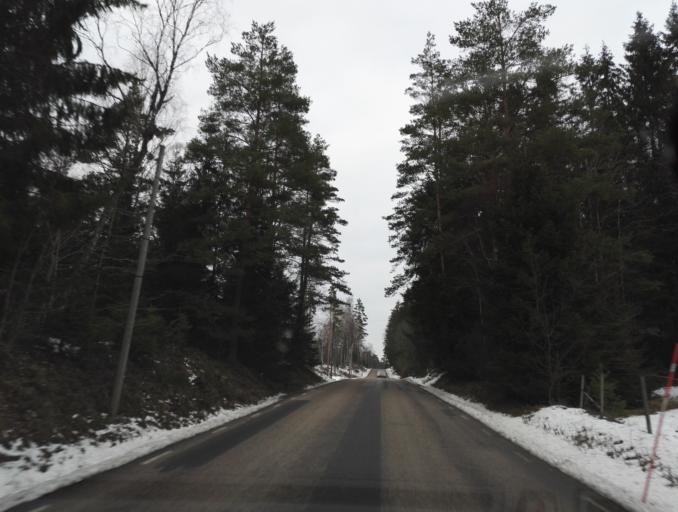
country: SE
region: Vaestra Goetaland
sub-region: Bollebygds Kommun
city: Bollebygd
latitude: 57.7385
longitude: 12.5964
